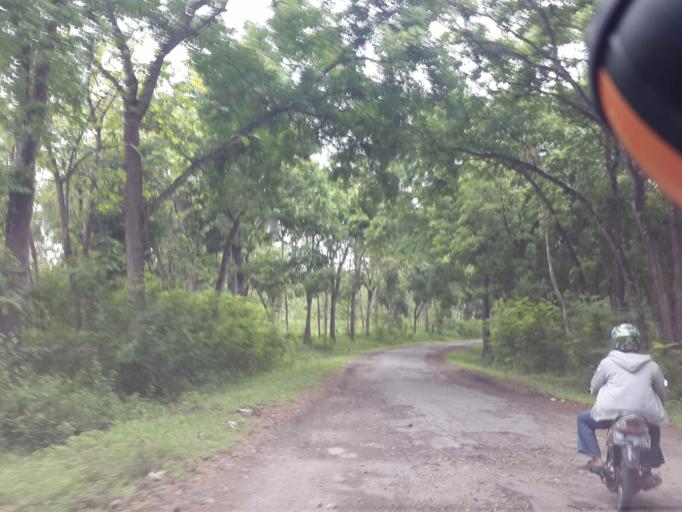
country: ID
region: East Java
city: Ponorogo
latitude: -7.7759
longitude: 111.3539
